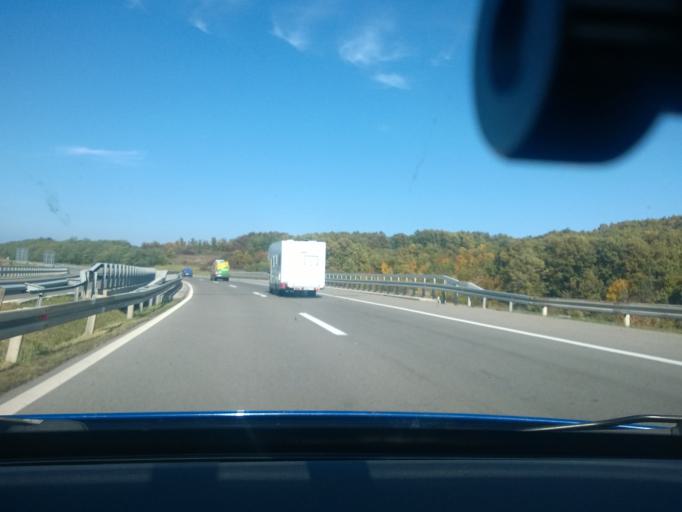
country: RS
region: Central Serbia
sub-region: Nisavski Okrug
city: Razanj
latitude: 43.6956
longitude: 21.5472
